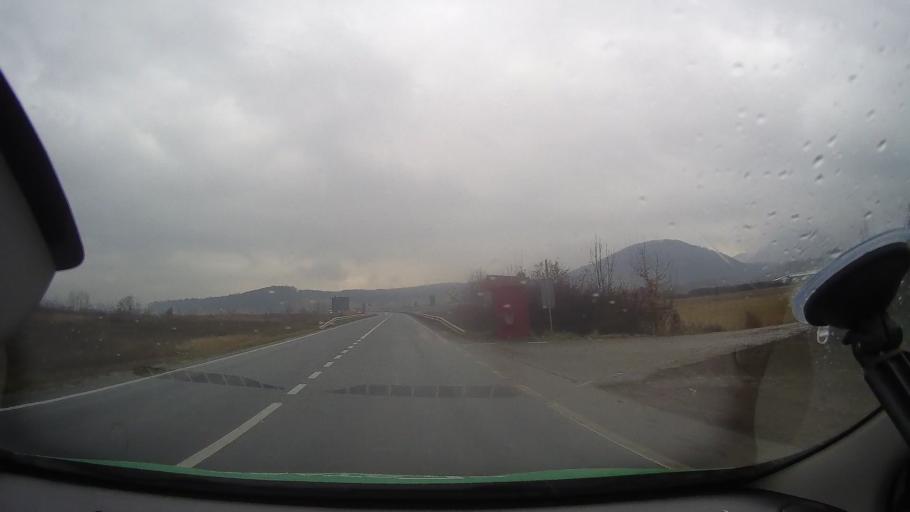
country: RO
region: Hunedoara
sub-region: Comuna Baia de Cris
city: Baia de Cris
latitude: 46.1803
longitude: 22.6817
